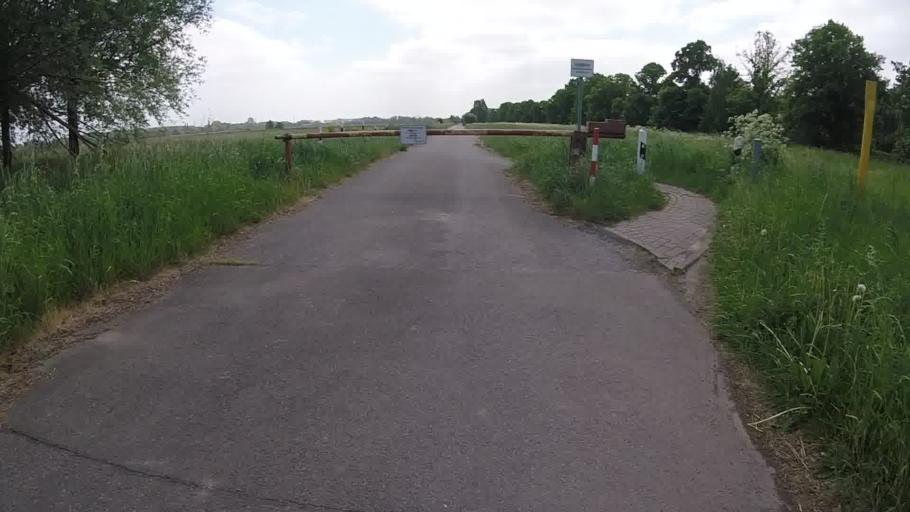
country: DE
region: Hamburg
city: Wandsbek
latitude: 53.5080
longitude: 10.1142
